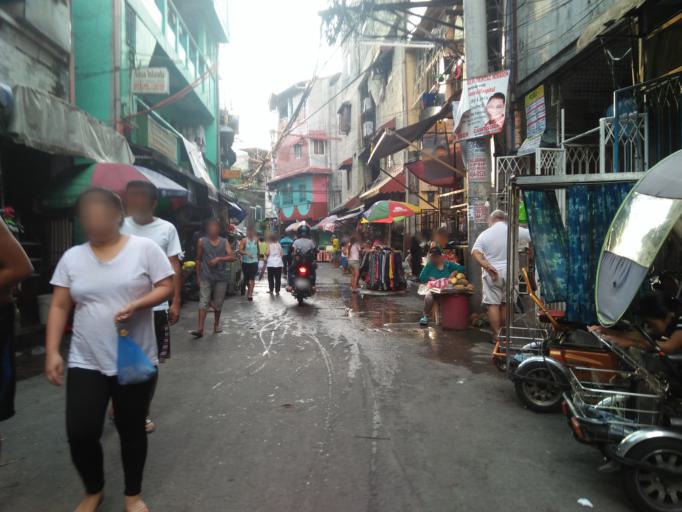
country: PH
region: Metro Manila
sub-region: San Juan
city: San Juan
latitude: 14.6000
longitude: 121.0197
